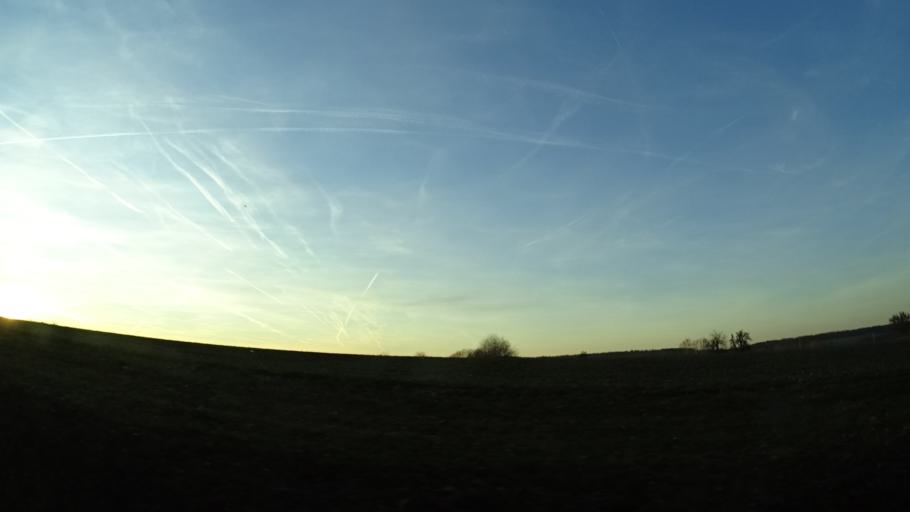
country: DE
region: Bavaria
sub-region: Regierungsbezirk Unterfranken
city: Geiselbach
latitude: 50.0978
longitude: 9.1903
